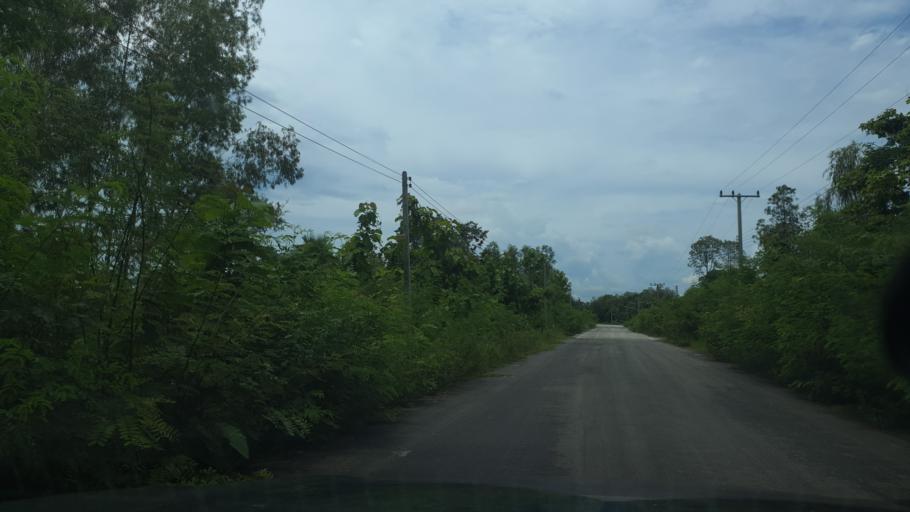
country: TH
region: Lampang
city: Ko Kha
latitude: 18.2487
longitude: 99.3678
